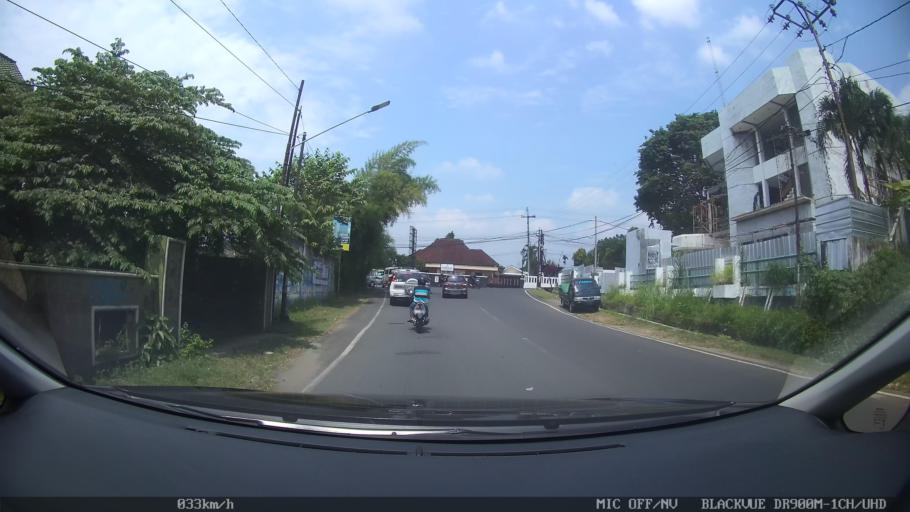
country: ID
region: Lampung
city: Bandarlampung
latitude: -5.4291
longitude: 105.2530
